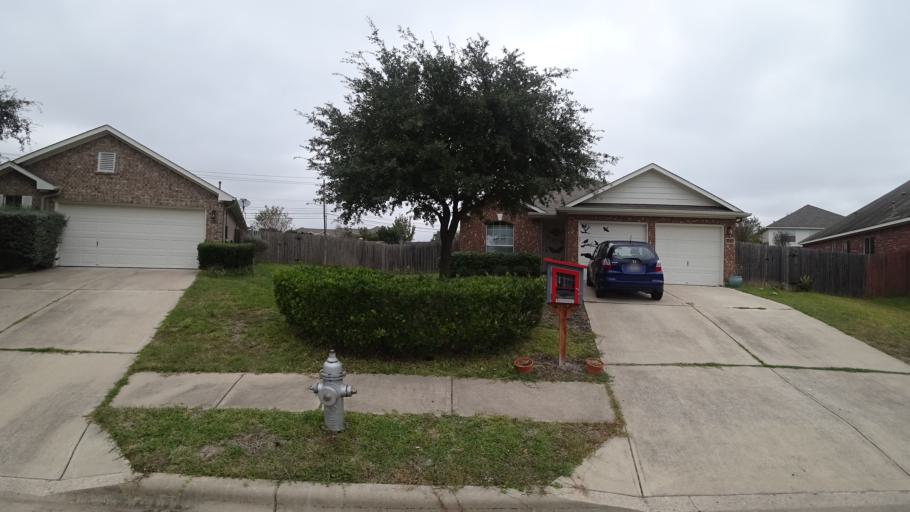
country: US
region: Texas
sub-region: Travis County
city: Pflugerville
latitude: 30.3777
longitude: -97.6566
